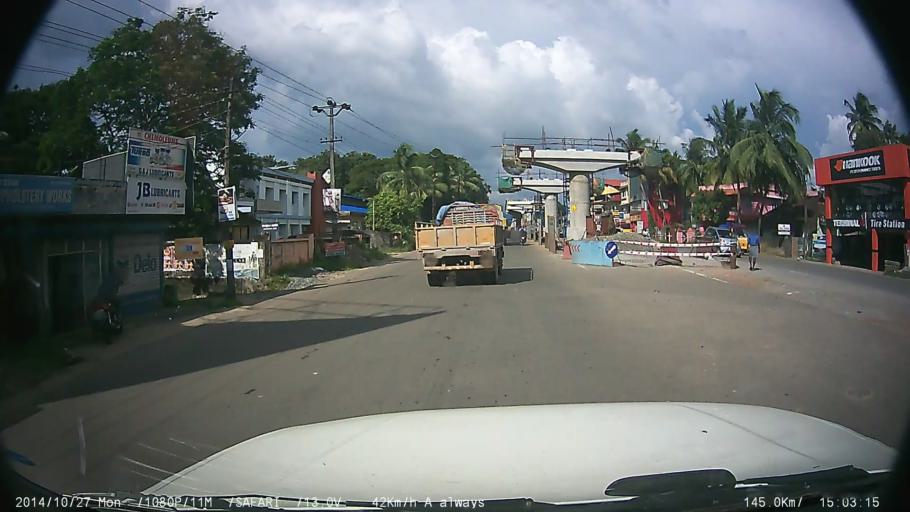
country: IN
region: Kerala
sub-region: Ernakulam
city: Aluva
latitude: 10.0895
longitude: 76.3440
